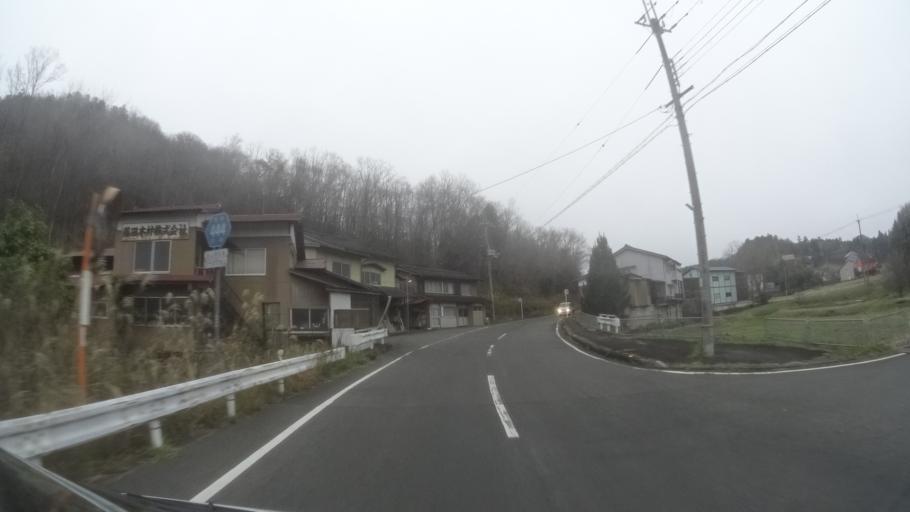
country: JP
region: Kyoto
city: Ayabe
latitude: 35.1765
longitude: 135.3770
